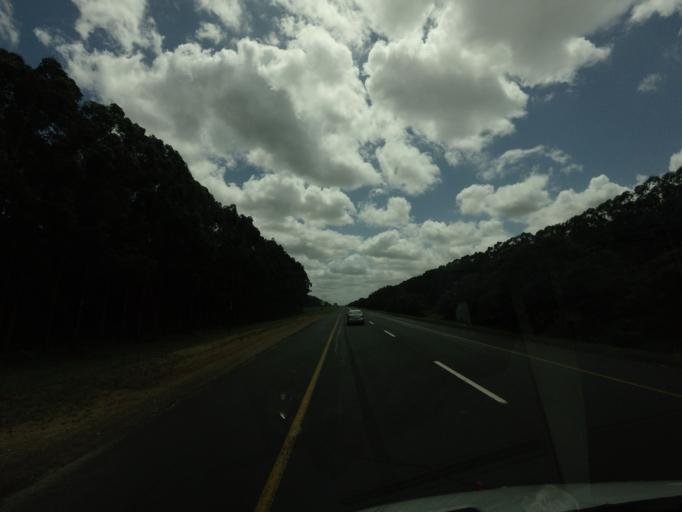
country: ZA
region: KwaZulu-Natal
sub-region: uThungulu District Municipality
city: KwaMbonambi
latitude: -28.5367
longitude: 32.1306
